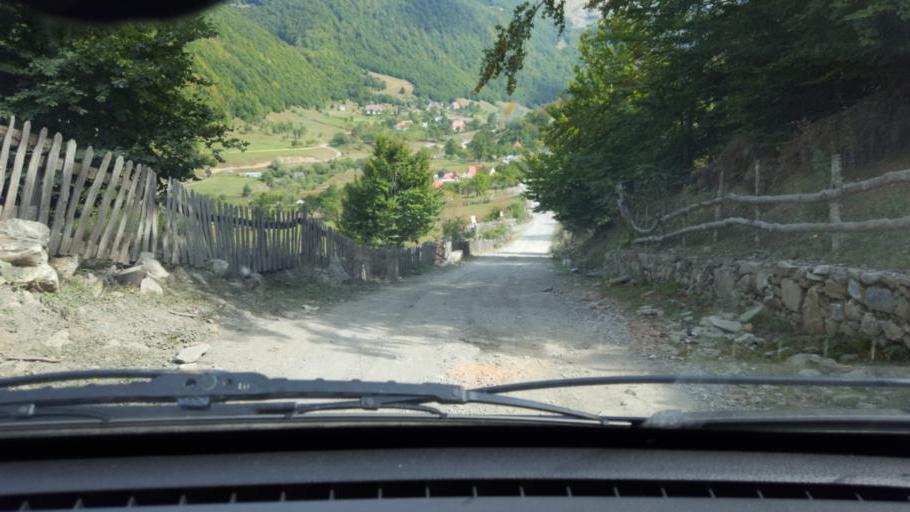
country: AL
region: Kukes
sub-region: Rrethi i Tropojes
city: Valbone
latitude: 42.5305
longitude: 19.7233
